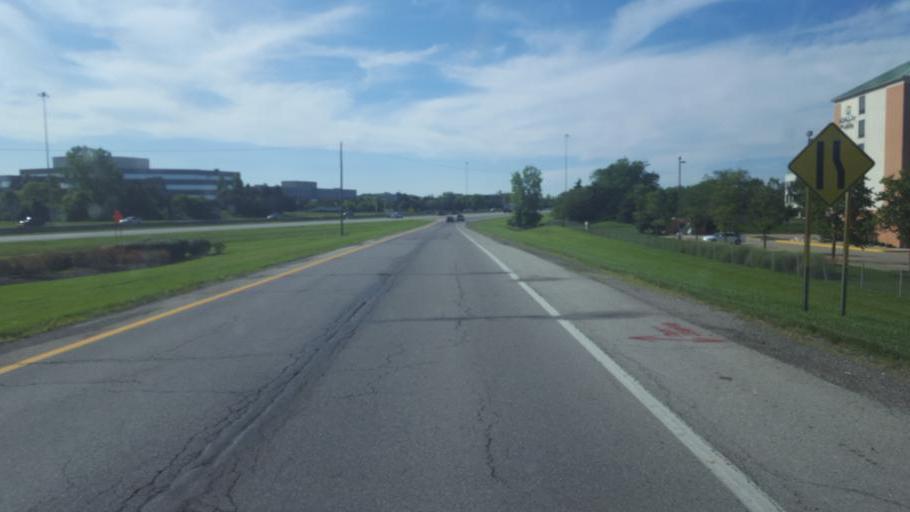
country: US
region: Ohio
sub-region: Franklin County
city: Dublin
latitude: 40.0770
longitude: -83.1349
